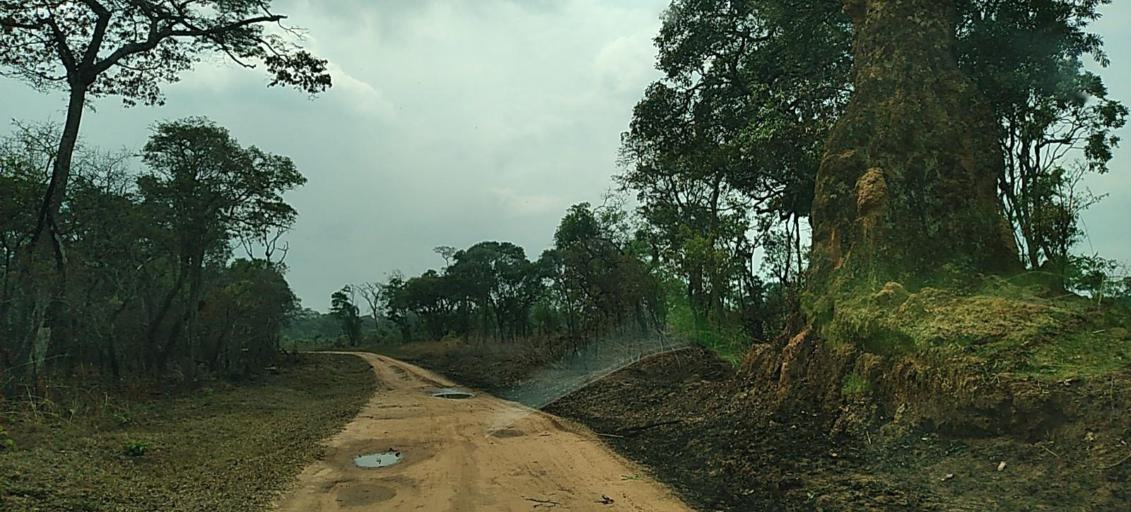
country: ZM
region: North-Western
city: Mwinilunga
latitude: -11.4673
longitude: 24.4792
